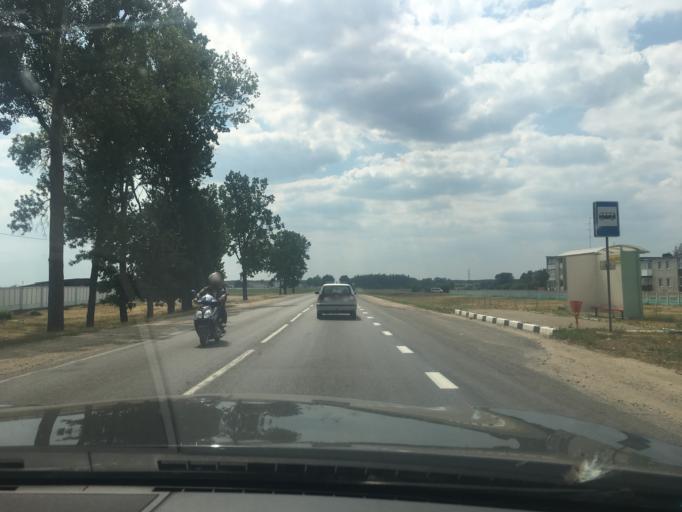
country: BY
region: Brest
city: Pruzhany
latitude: 52.5475
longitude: 24.4620
